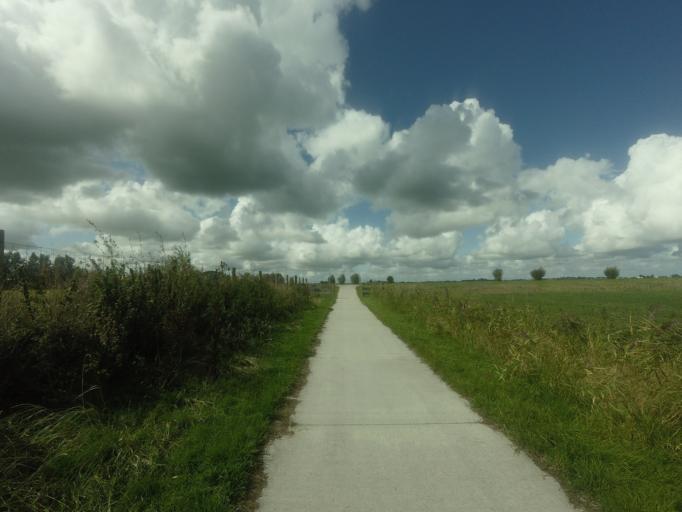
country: NL
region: Friesland
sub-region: Gemeente Littenseradiel
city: Makkum
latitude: 53.0898
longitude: 5.7045
